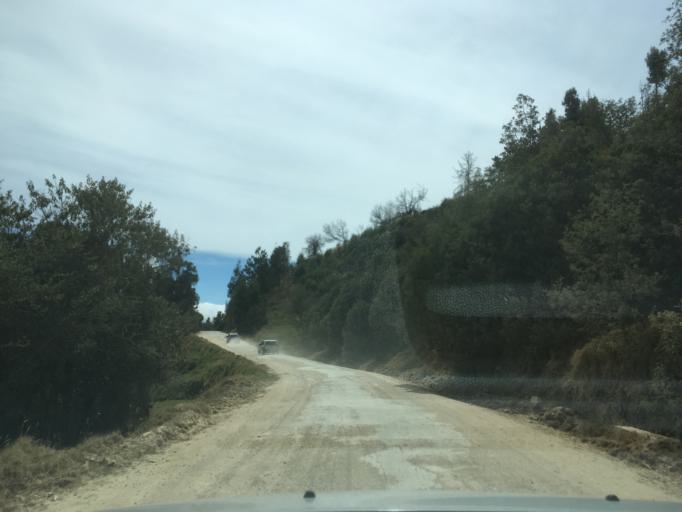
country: CO
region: Boyaca
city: Aquitania
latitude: 5.5894
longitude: -72.9213
